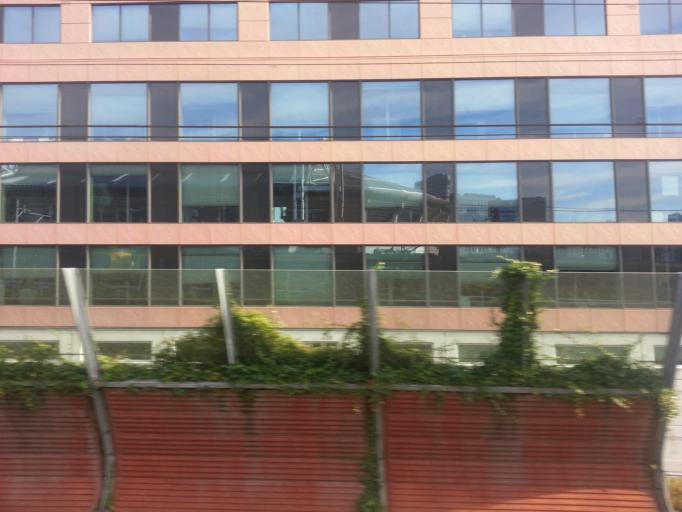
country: NL
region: North Holland
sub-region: Gemeente Ouder-Amstel
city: Duivendrecht
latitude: 52.3148
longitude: 4.9452
